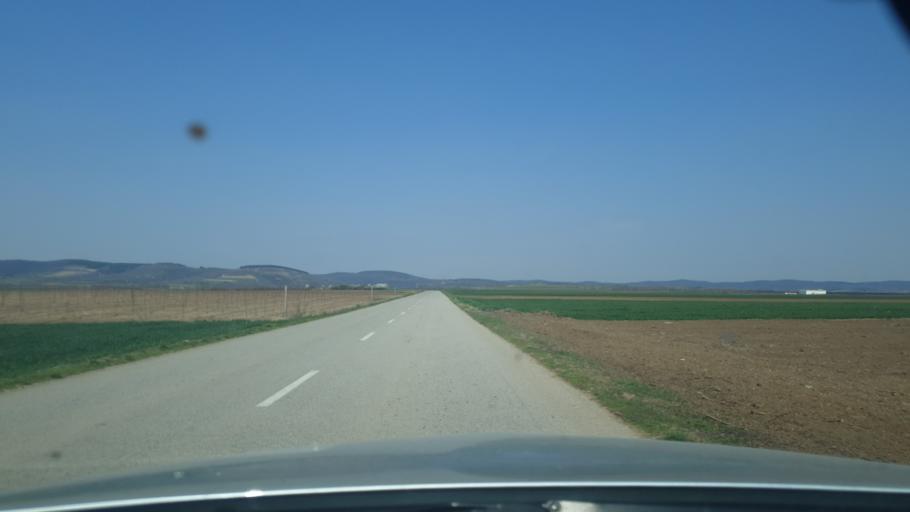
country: RS
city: Vrdnik
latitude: 45.0788
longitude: 19.7697
